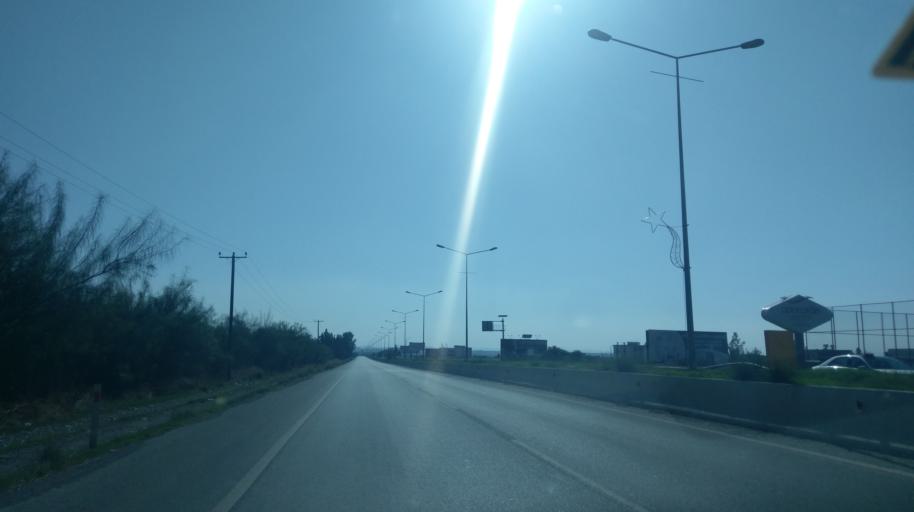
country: CY
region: Lefkosia
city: Geri
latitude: 35.2077
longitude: 33.4989
